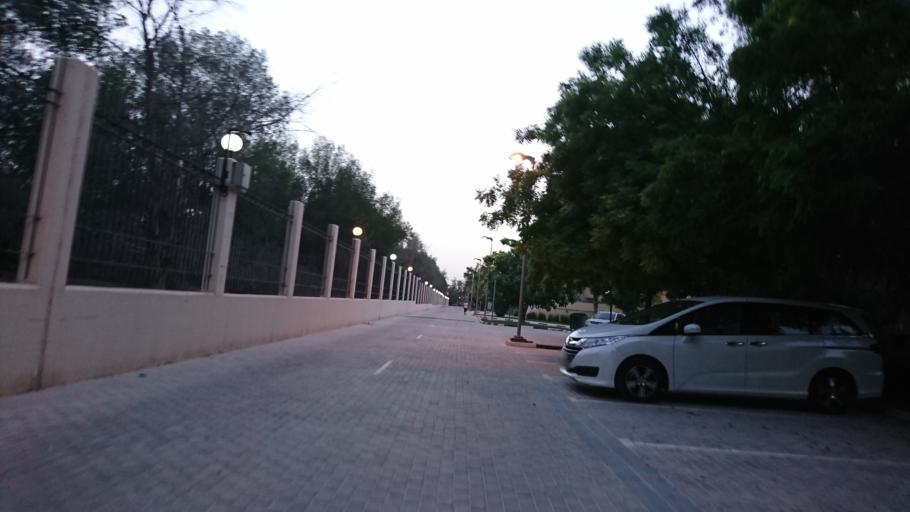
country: QA
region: Baladiyat ad Dawhah
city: Doha
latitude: 25.3836
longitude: 51.5145
